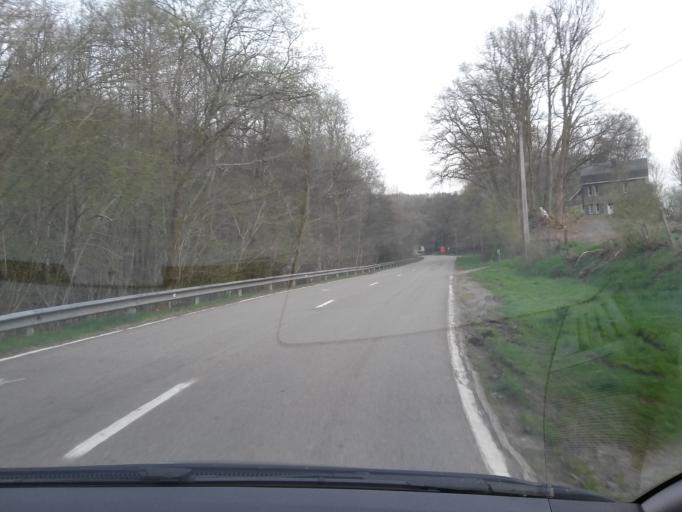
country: BE
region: Wallonia
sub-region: Province du Luxembourg
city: Herbeumont
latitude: 49.8037
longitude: 5.2166
